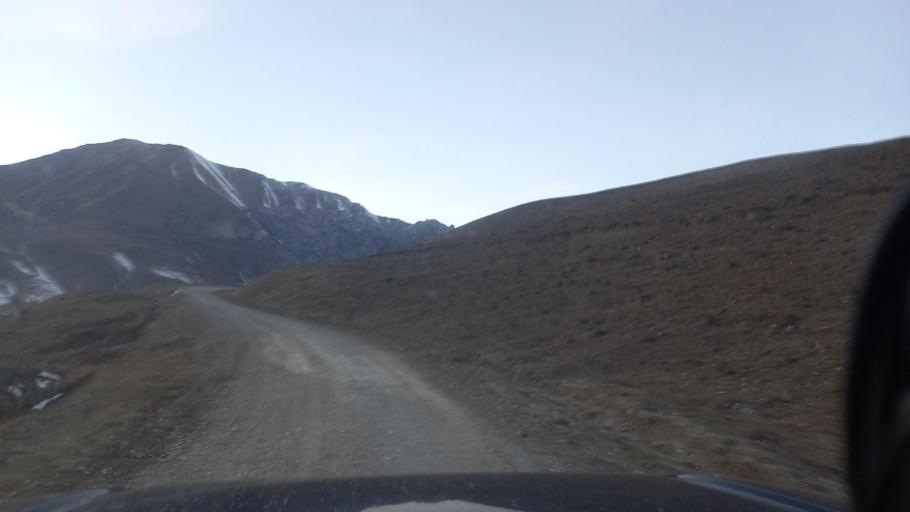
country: RU
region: Ingushetiya
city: Dzhayrakh
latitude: 42.8391
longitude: 44.5421
